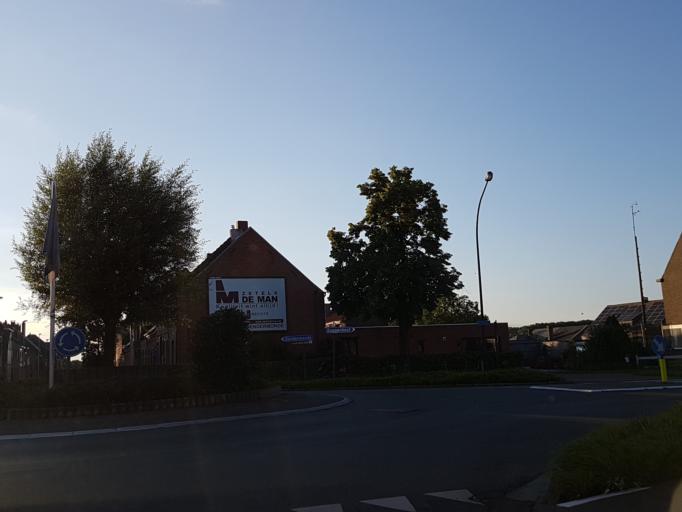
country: BE
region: Flanders
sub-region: Provincie Oost-Vlaanderen
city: Lebbeke
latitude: 51.0034
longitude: 4.1256
